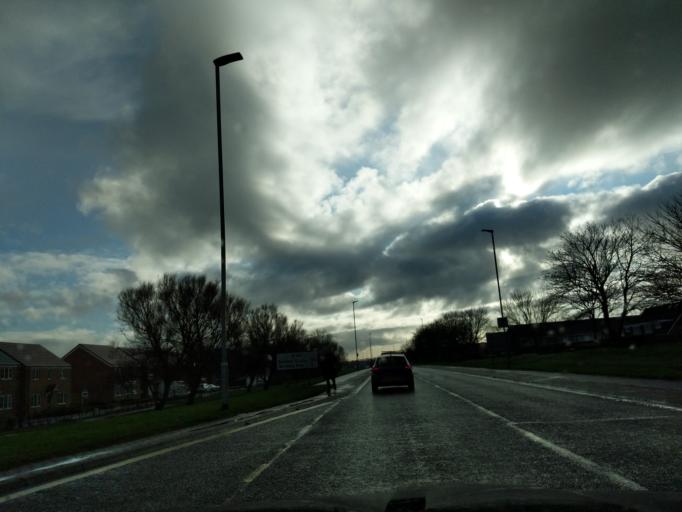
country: GB
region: England
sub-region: Northumberland
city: Blyth
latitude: 55.1142
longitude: -1.5063
